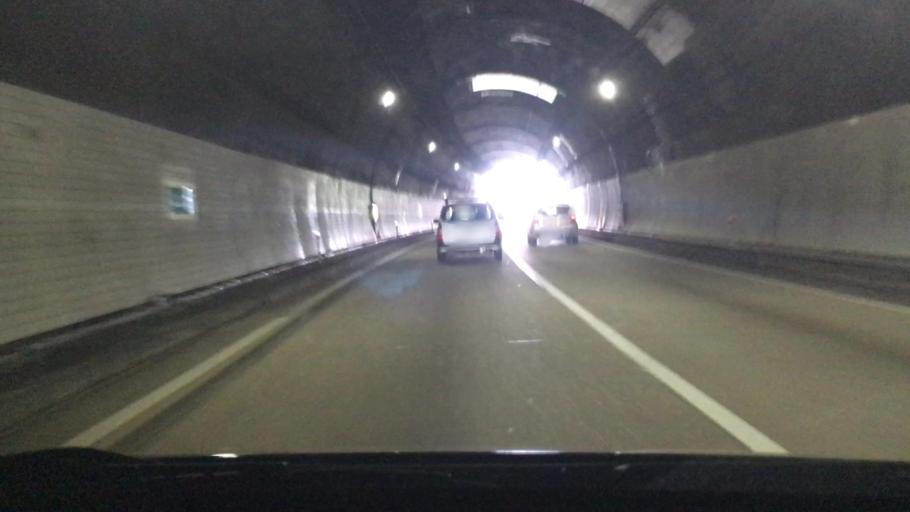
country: JP
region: Hiroshima
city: Hatsukaichi
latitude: 34.3807
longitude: 132.3905
